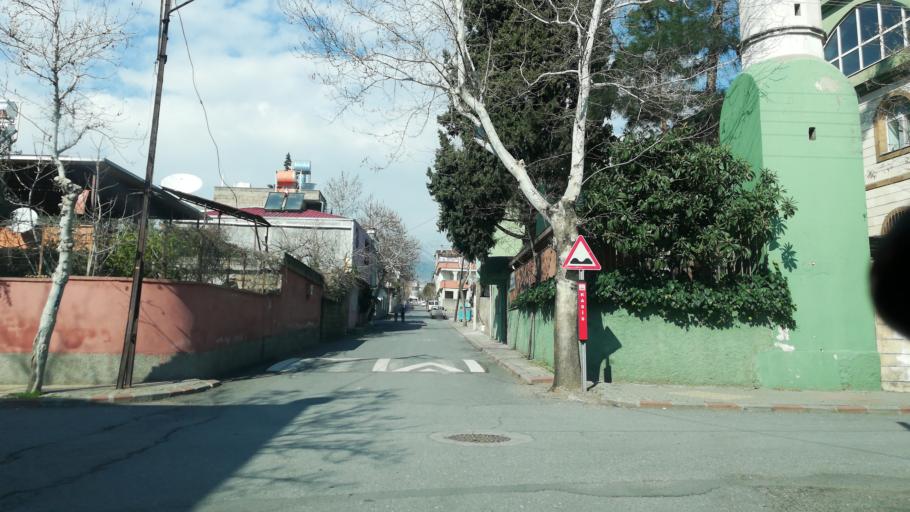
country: TR
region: Kahramanmaras
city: Kahramanmaras
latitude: 37.5719
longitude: 36.9484
